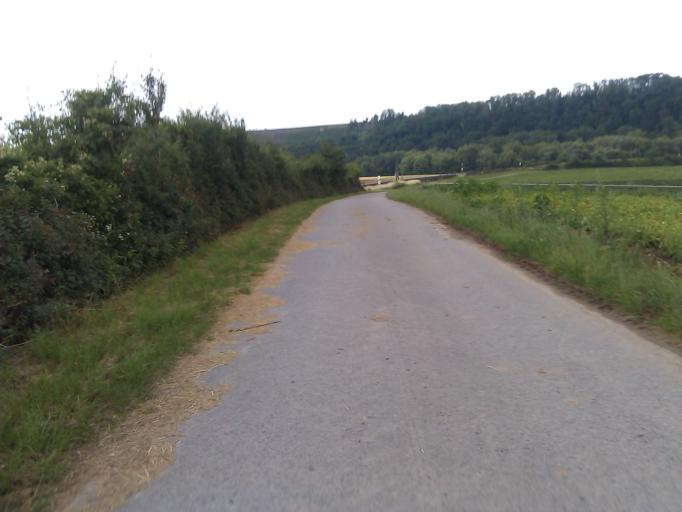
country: DE
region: Baden-Wuerttemberg
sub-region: Regierungsbezirk Stuttgart
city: Kirchheim am Neckar
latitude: 49.0592
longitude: 9.1420
